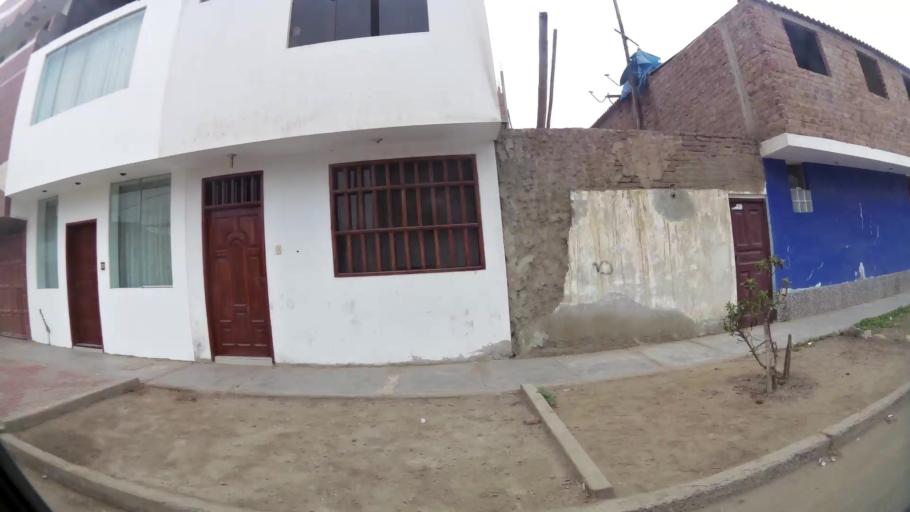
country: PE
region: La Libertad
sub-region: Provincia de Trujillo
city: Buenos Aires
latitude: -8.1461
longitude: -79.0495
